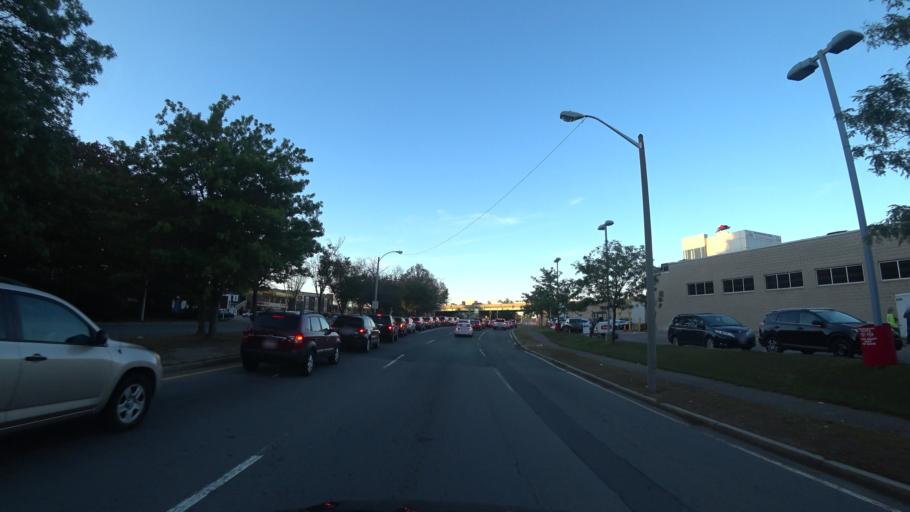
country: US
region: Massachusetts
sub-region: Suffolk County
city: South Boston
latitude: 42.2994
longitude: -71.0495
